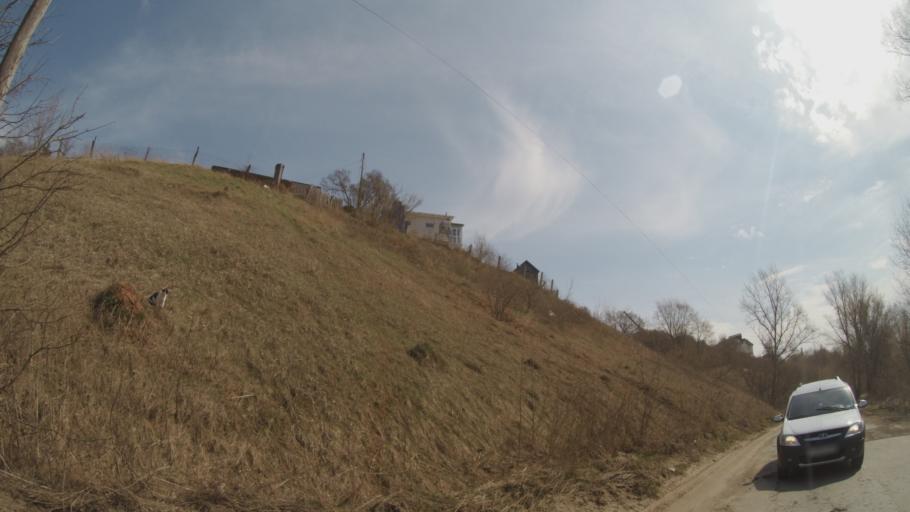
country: RU
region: Nizjnij Novgorod
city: Vyyezdnoye
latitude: 55.3916
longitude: 43.8076
